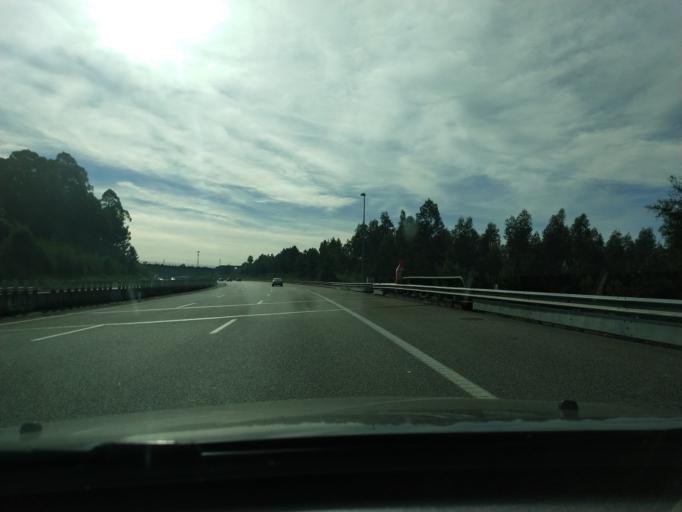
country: PT
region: Aveiro
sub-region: Ovar
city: Sao Joao
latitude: 40.8874
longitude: -8.5670
